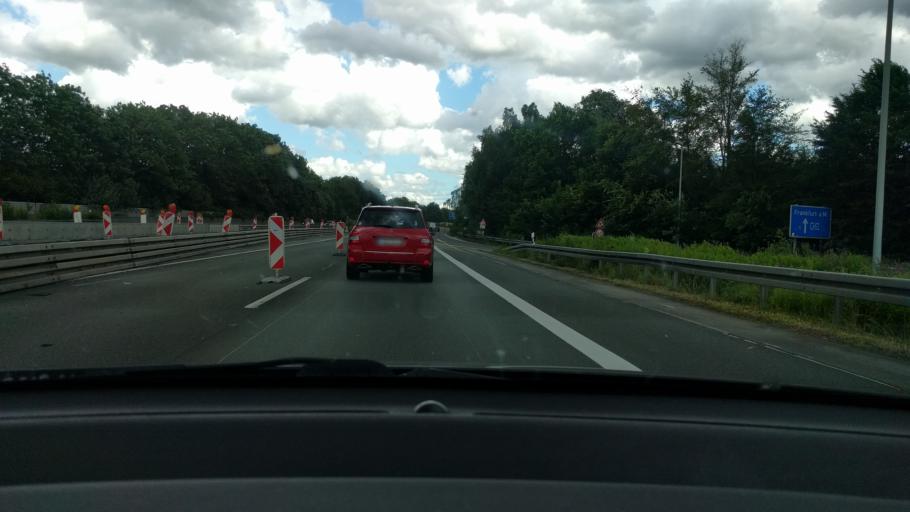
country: DE
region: North Rhine-Westphalia
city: Castrop-Rauxel
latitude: 51.5358
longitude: 7.3704
